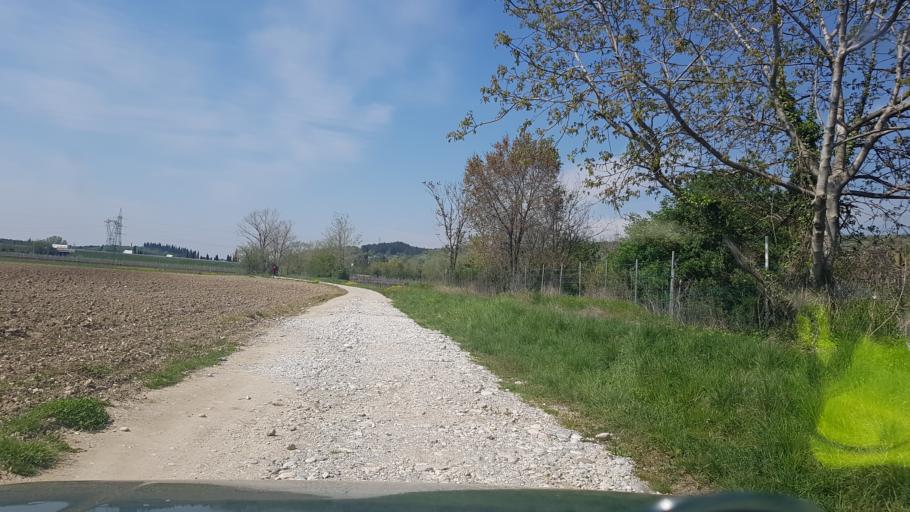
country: IT
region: Friuli Venezia Giulia
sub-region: Provincia di Gorizia
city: Ronchi dei Legionari
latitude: 45.8392
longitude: 13.4999
